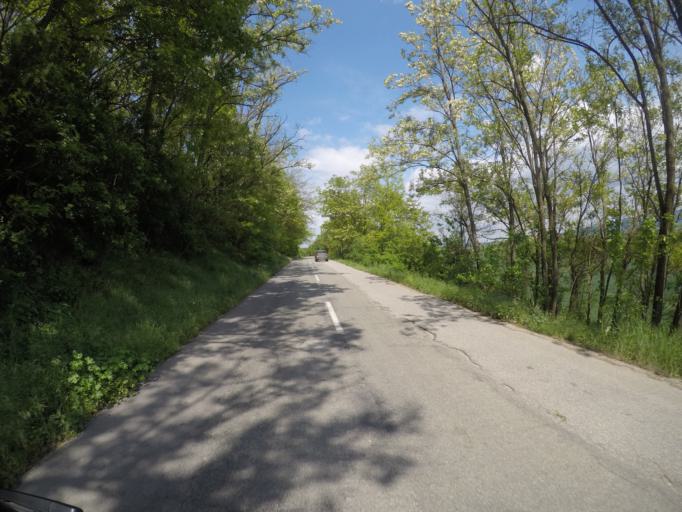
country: SK
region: Nitriansky
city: Zeliezovce
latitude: 47.9500
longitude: 18.7401
